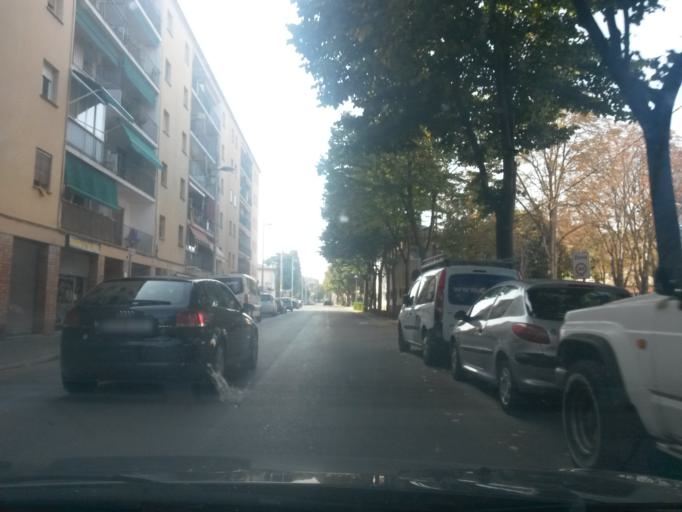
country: ES
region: Catalonia
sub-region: Provincia de Girona
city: Girona
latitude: 41.9737
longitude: 2.8130
